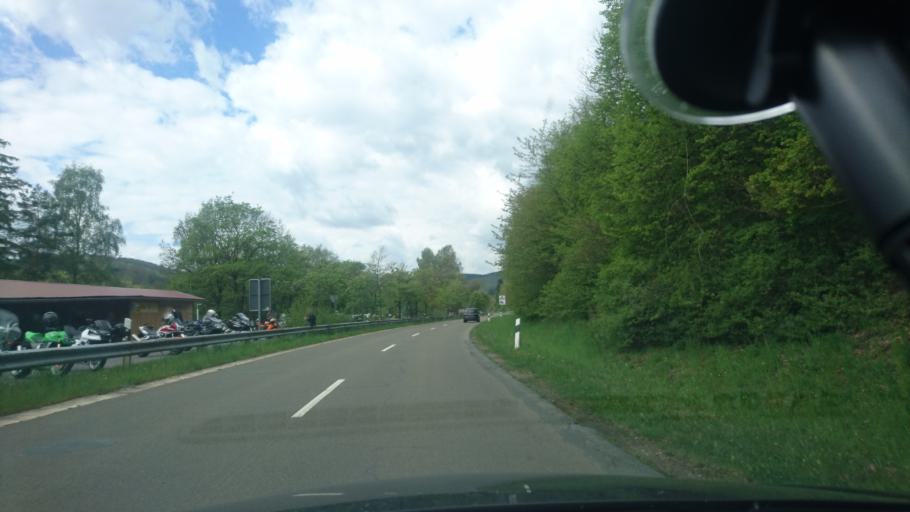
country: DE
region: Hesse
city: Willingen
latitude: 51.3737
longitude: 8.7207
